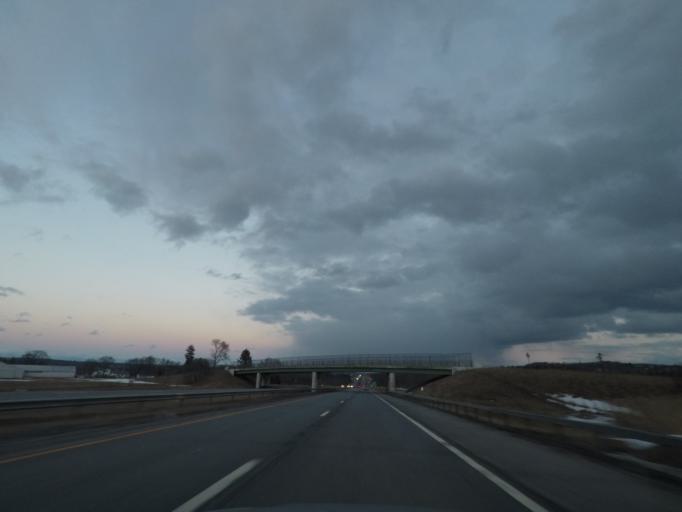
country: US
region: New York
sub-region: Montgomery County
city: Amsterdam
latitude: 42.9293
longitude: -74.2267
